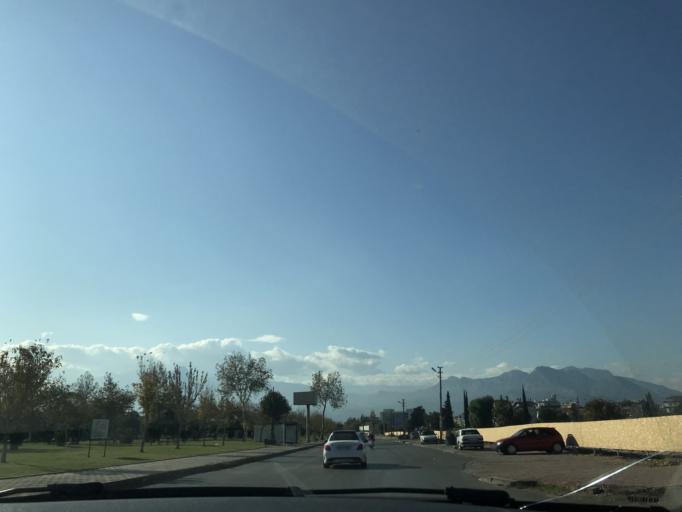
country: TR
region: Antalya
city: Antalya
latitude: 36.9020
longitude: 30.6510
